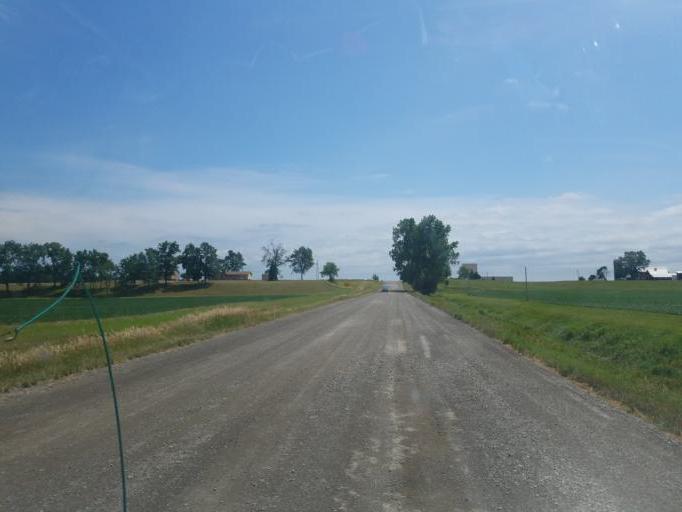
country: US
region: Indiana
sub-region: Allen County
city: Woodburn
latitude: 41.1668
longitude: -84.8490
